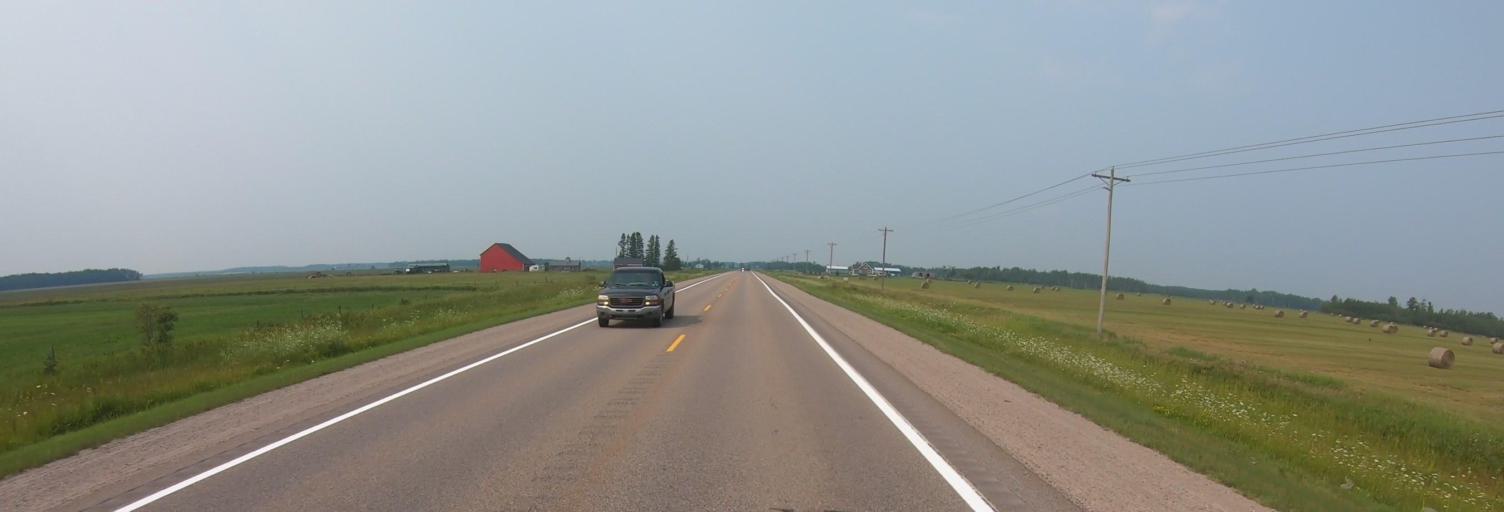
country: US
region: Michigan
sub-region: Chippewa County
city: Sault Ste. Marie
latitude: 46.3530
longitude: -84.3640
